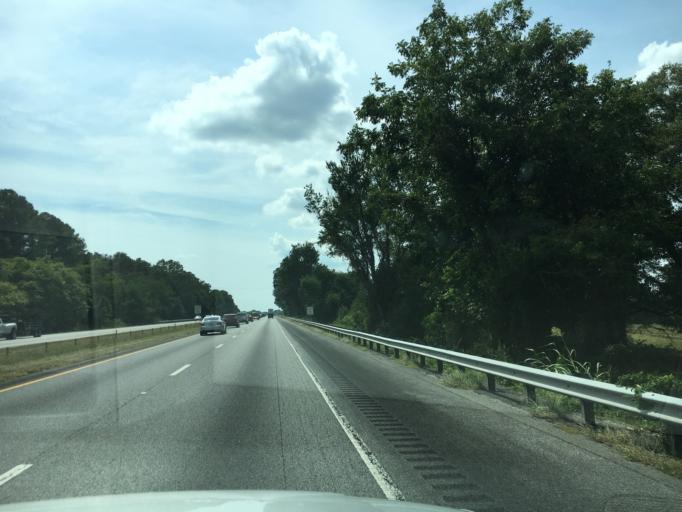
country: US
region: South Carolina
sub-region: Anderson County
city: Centerville
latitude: 34.5567
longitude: -82.7780
